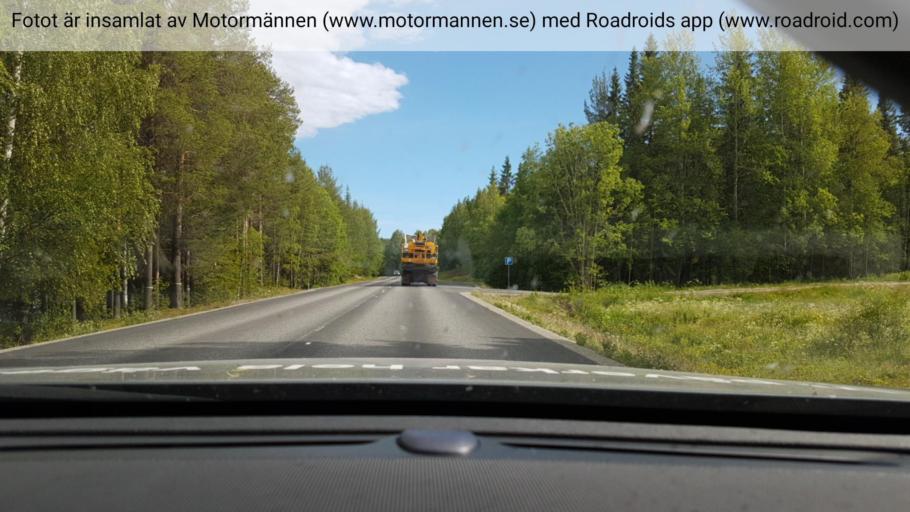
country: SE
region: Vaesterbotten
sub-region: Lycksele Kommun
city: Soderfors
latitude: 64.8600
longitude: 17.9312
